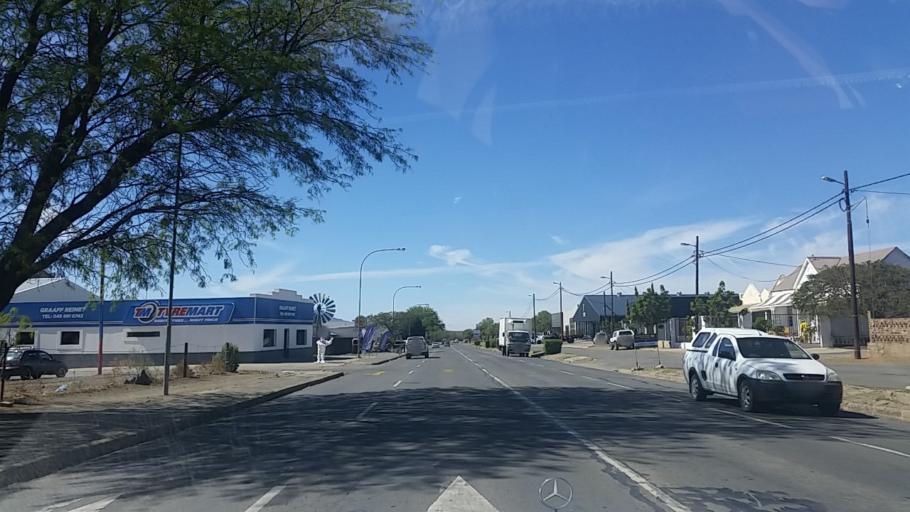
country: ZA
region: Eastern Cape
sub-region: Cacadu District Municipality
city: Graaff-Reinet
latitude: -32.2653
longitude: 24.5421
